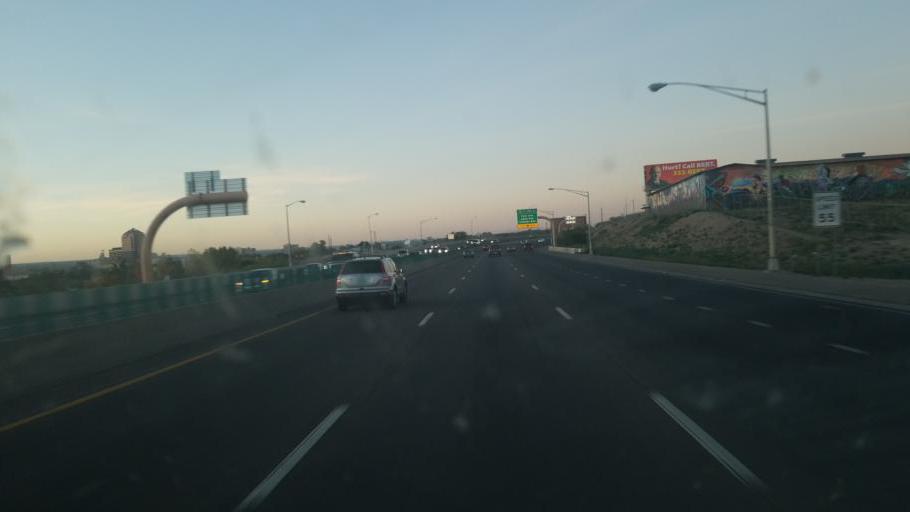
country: US
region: New Mexico
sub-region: Bernalillo County
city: Albuquerque
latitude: 35.0722
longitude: -106.6399
